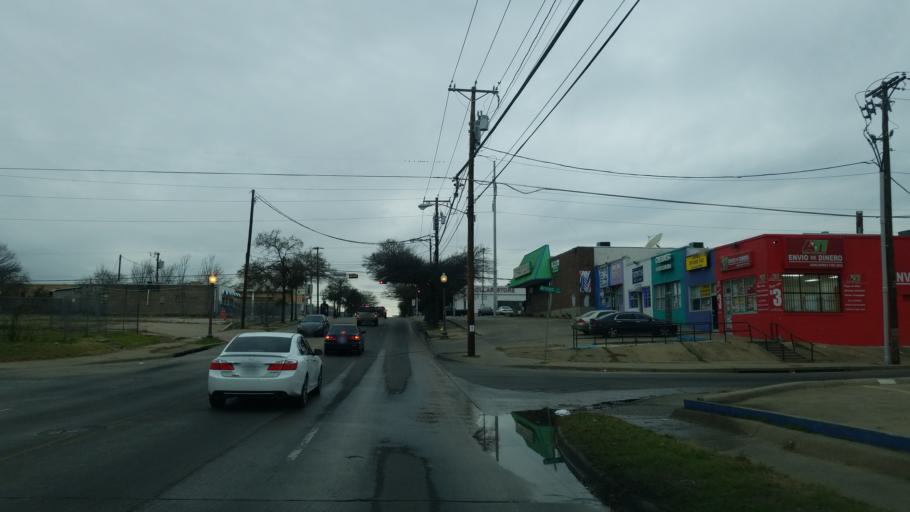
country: US
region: Texas
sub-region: Dallas County
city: Dallas
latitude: 32.8108
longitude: -96.8217
